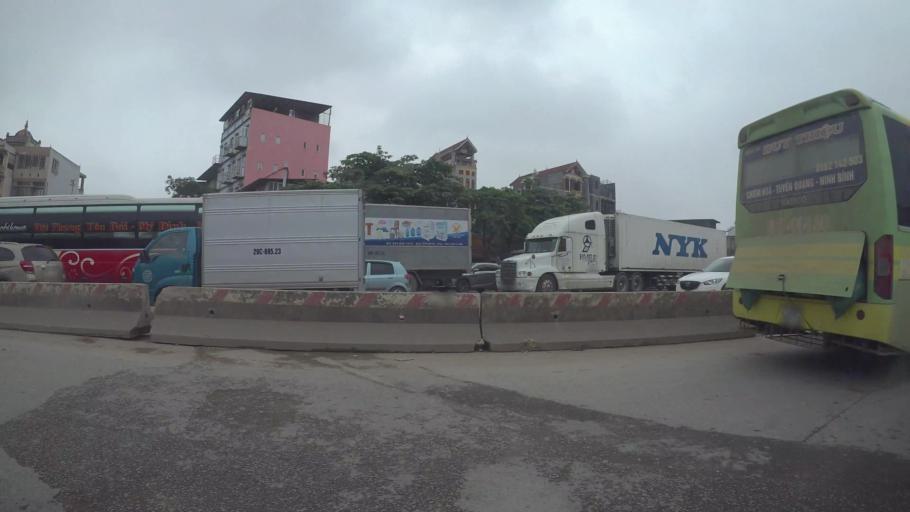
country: VN
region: Ha Noi
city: Tay Ho
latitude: 21.0769
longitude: 105.7862
